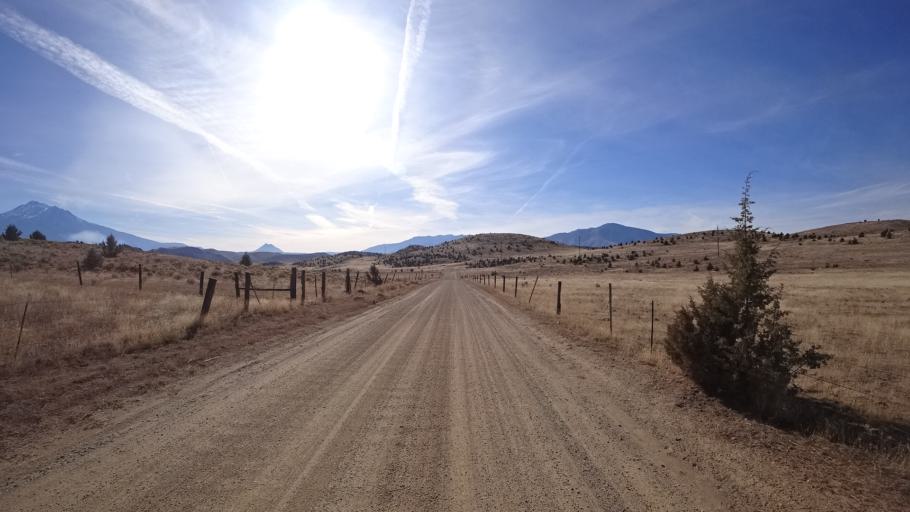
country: US
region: California
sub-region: Siskiyou County
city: Weed
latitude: 41.5487
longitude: -122.4753
